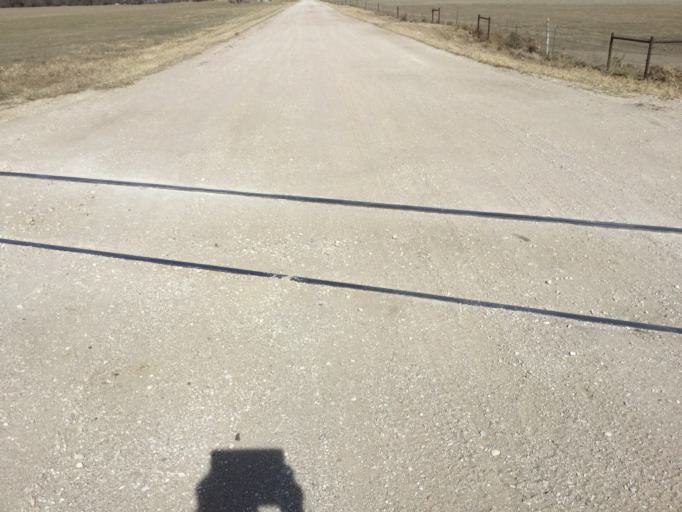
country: US
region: Kansas
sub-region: Rice County
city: Sterling
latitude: 38.2345
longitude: -98.2892
